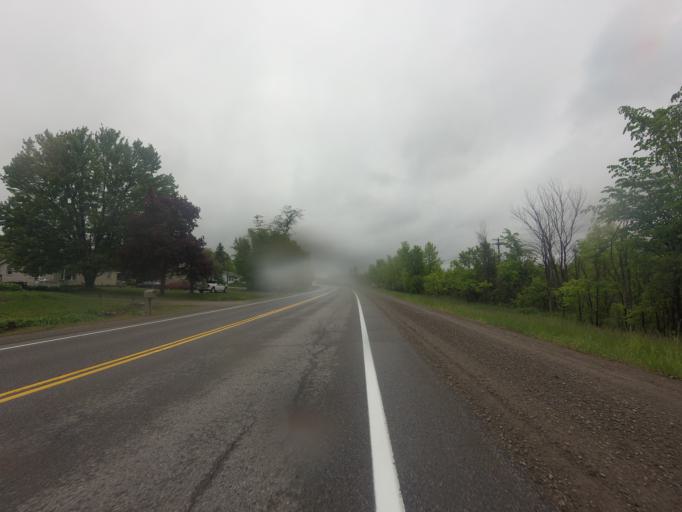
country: CA
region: Ontario
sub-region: Lanark County
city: Smiths Falls
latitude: 44.8515
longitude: -76.0552
